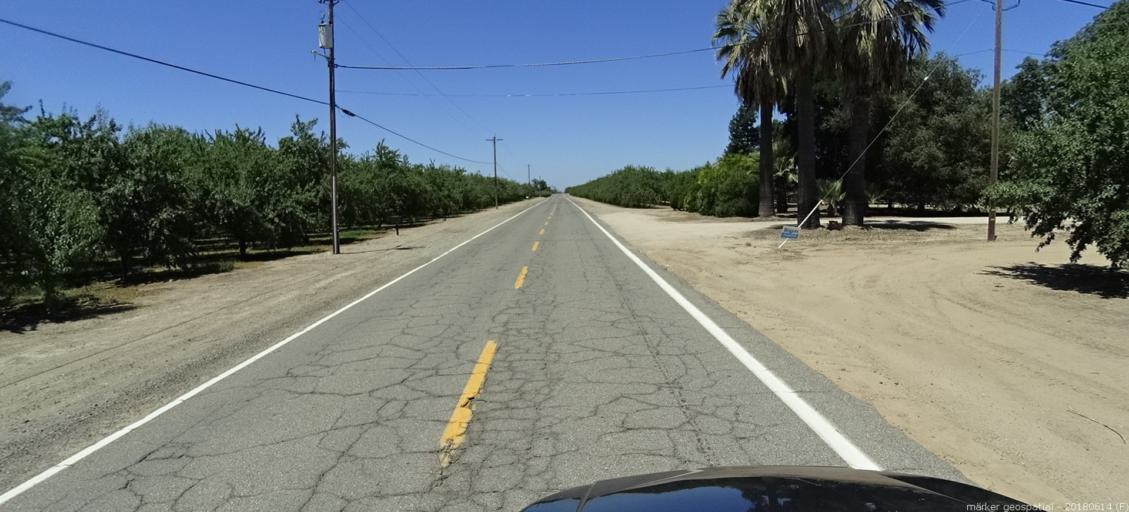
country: US
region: California
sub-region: Madera County
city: Fairmead
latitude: 37.0401
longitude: -120.1943
